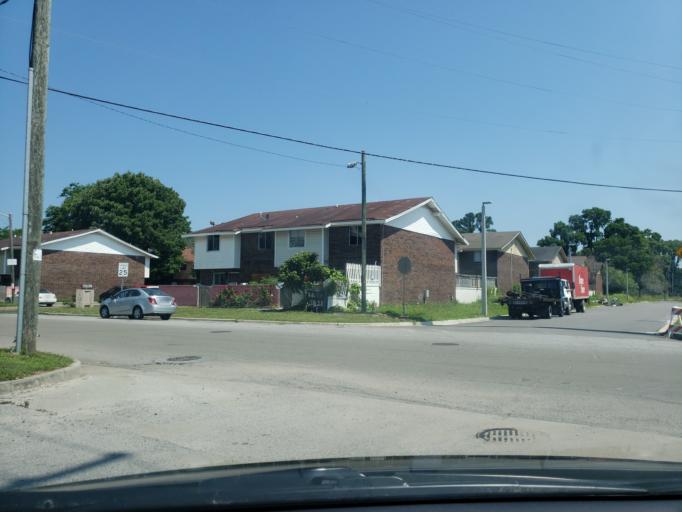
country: US
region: Georgia
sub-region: Chatham County
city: Montgomery
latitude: 31.9945
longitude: -81.1319
